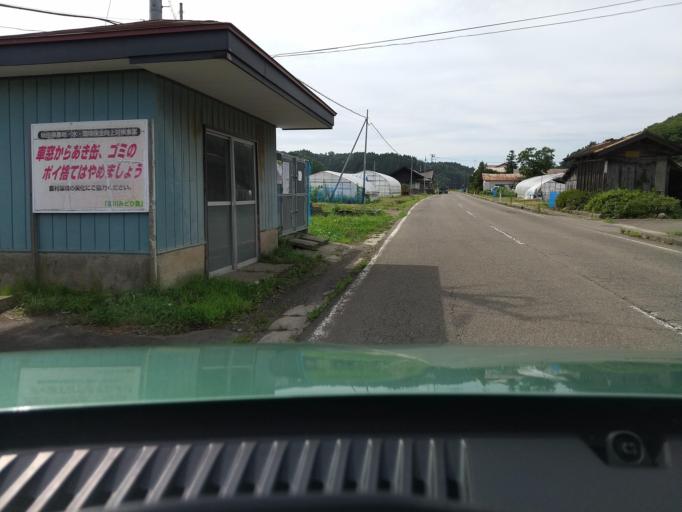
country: JP
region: Akita
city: Akita
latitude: 39.7823
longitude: 140.1301
